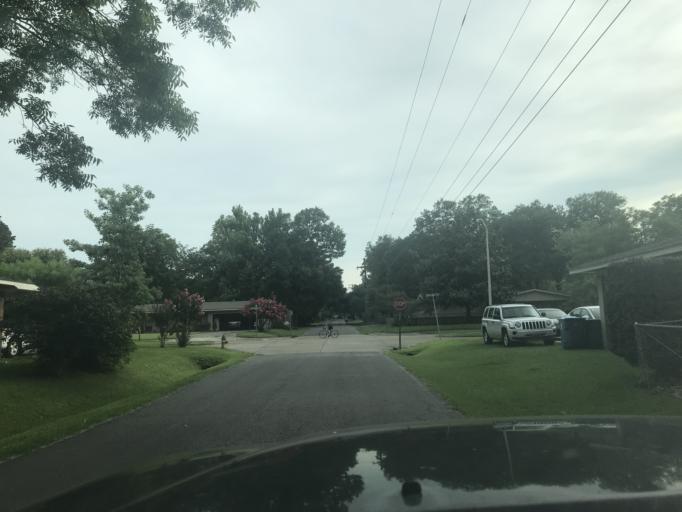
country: US
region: Louisiana
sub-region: Lafayette Parish
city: Lafayette
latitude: 30.1990
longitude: -92.0499
